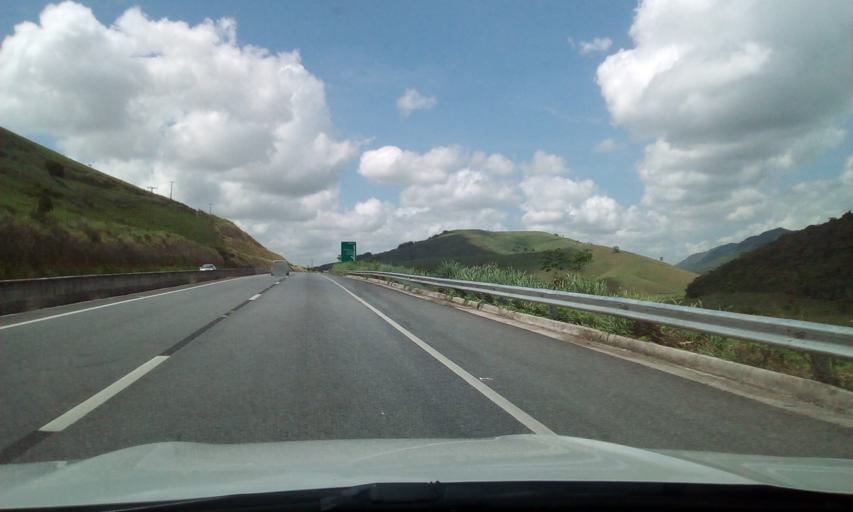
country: BR
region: Alagoas
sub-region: Flexeiras
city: Flexeiras
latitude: -9.2507
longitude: -35.7685
